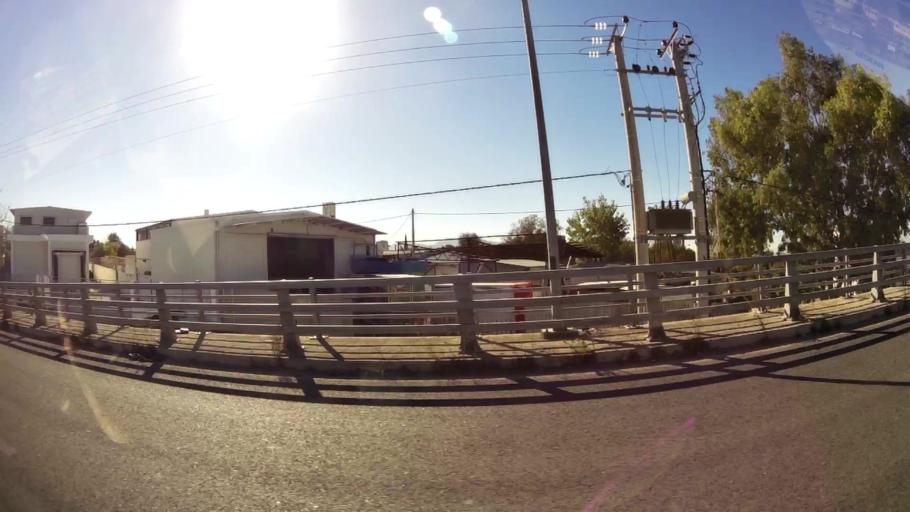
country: GR
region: Attica
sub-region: Nomarchia Athinas
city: Metamorfosi
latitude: 38.0924
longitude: 23.7716
